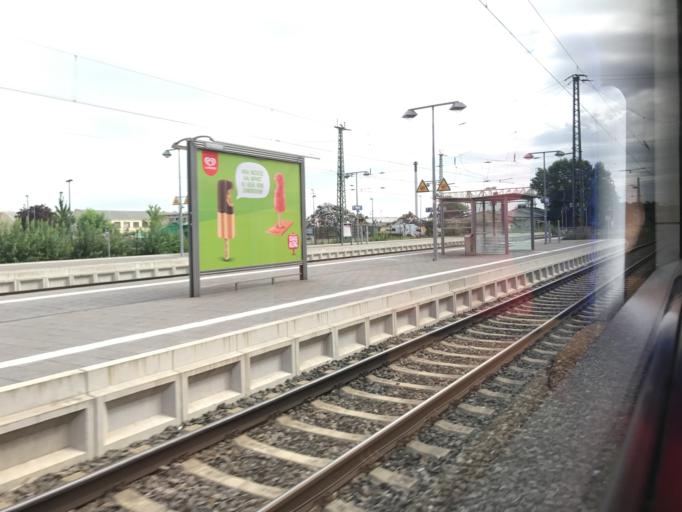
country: DE
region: Hesse
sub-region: Regierungsbezirk Giessen
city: Wetzlar
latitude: 50.5657
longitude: 8.5045
